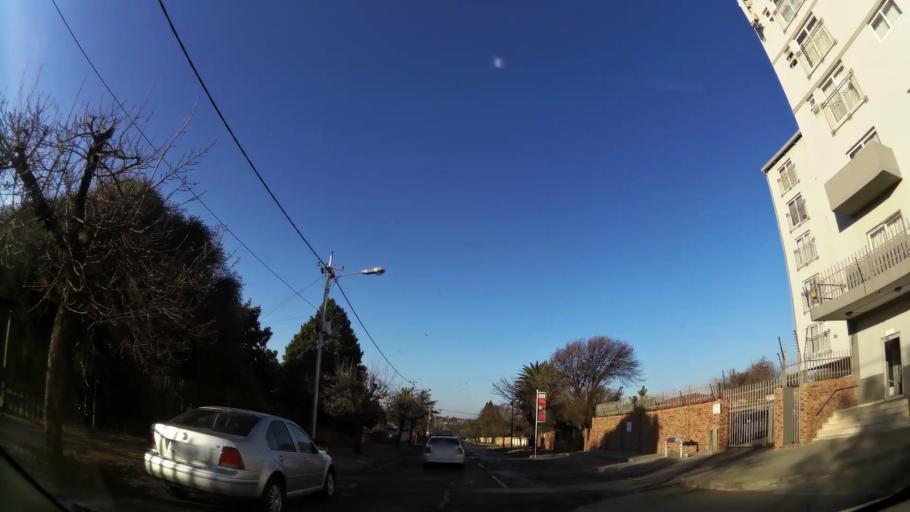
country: ZA
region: Gauteng
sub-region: City of Johannesburg Metropolitan Municipality
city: Roodepoort
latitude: -26.1846
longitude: 27.9216
